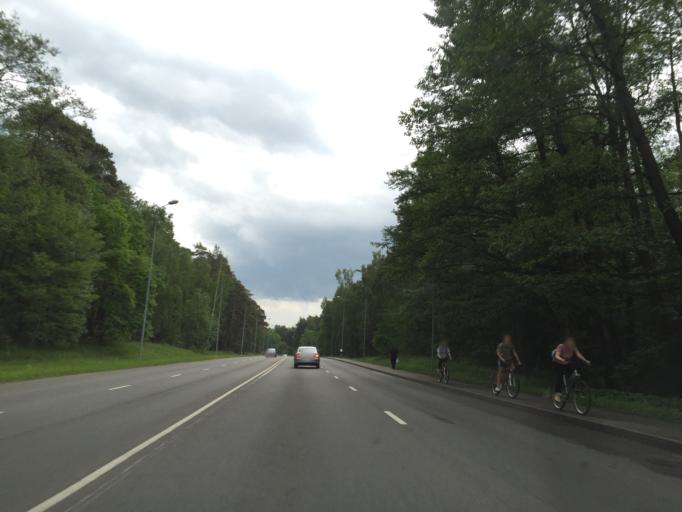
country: LT
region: Klaipedos apskritis
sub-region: Klaipeda
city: Klaipeda
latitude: 55.7365
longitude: 21.0979
